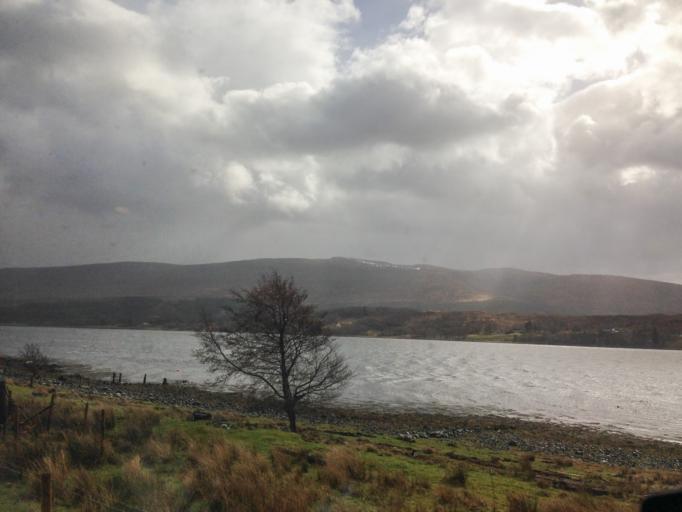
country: GB
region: Scotland
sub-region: Highland
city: Fort William
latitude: 56.8556
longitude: -5.2885
